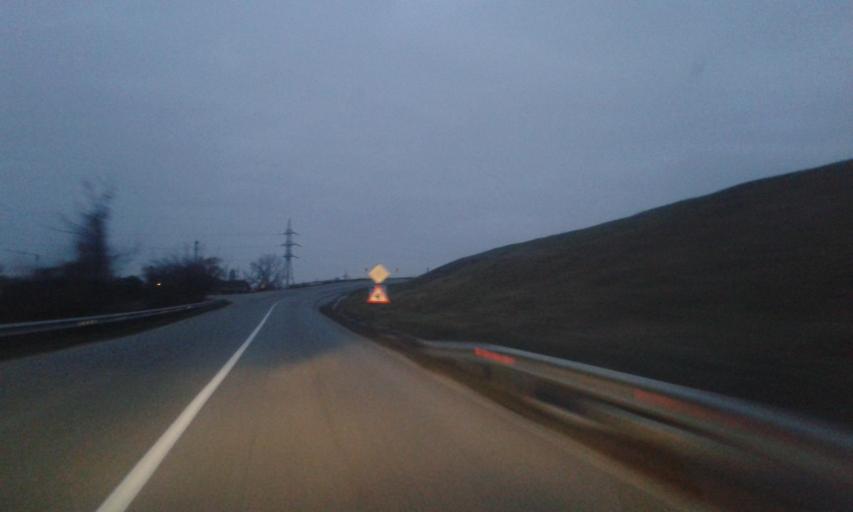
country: RO
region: Gorj
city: Targu Jiu
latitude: 45.0594
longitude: 23.2729
